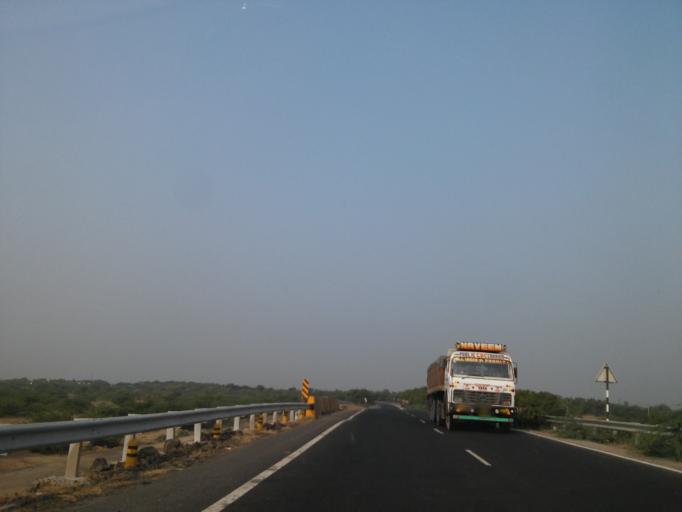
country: IN
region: Gujarat
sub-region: Kachchh
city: Anjar
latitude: 23.2924
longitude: 70.0427
